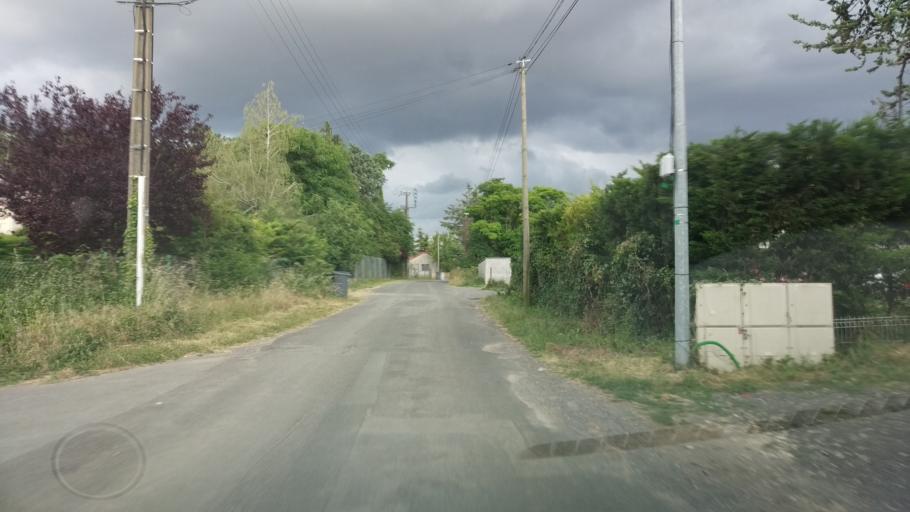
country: FR
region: Poitou-Charentes
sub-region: Departement de la Vienne
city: Migne-Auxances
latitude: 46.6252
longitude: 0.3452
